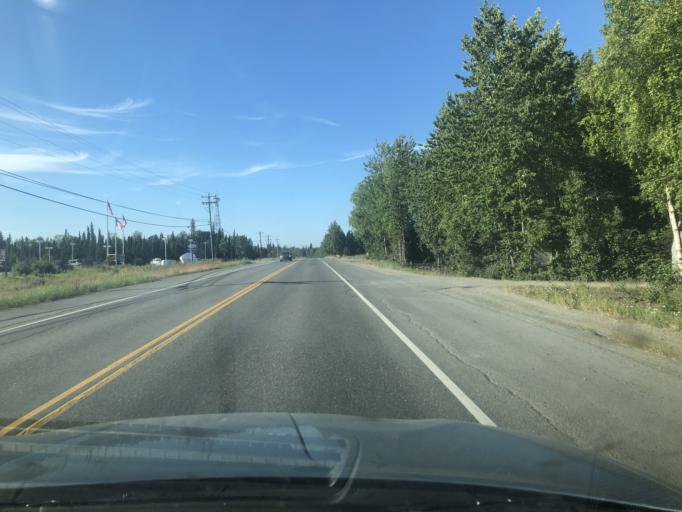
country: US
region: Alaska
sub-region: Kenai Peninsula Borough
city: Ridgeway
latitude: 60.5246
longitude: -151.0810
